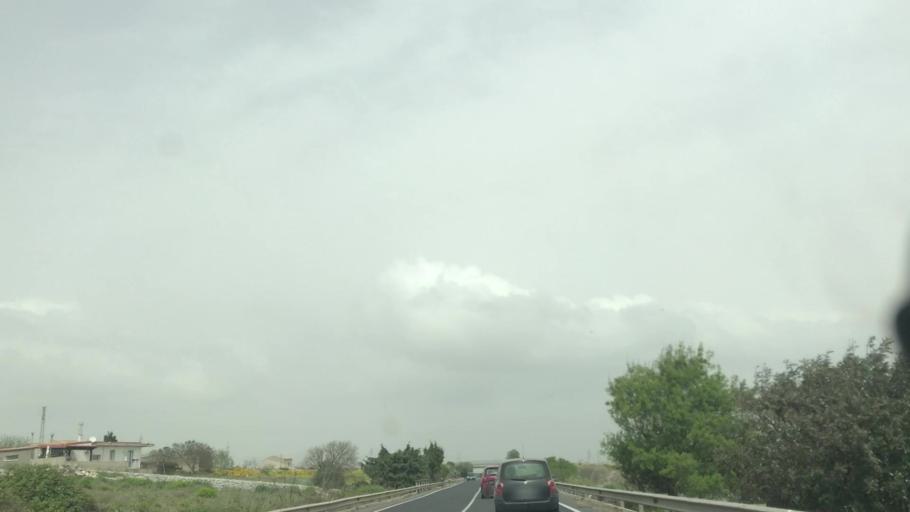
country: IT
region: Sicily
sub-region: Ragusa
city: Ragusa
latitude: 36.8741
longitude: 14.6909
